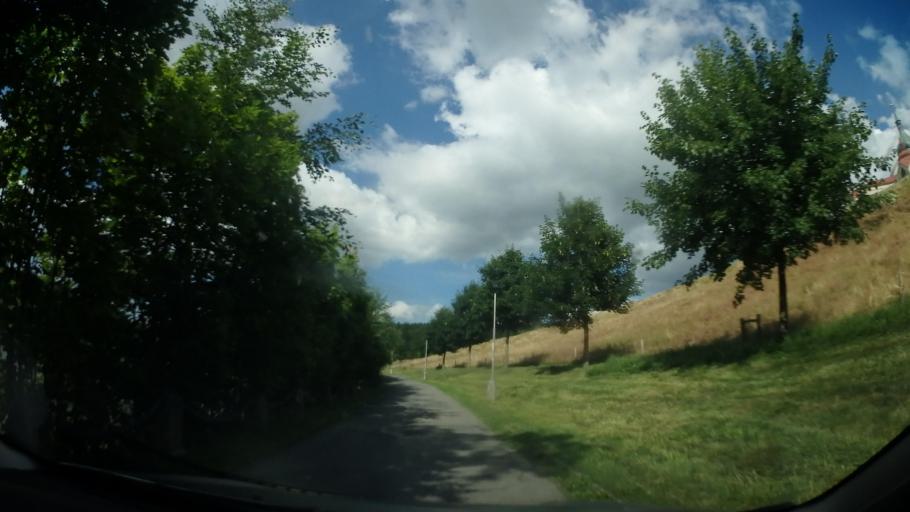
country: CZ
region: Vysocina
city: Zd'ar nad Sazavou Druhy
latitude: 49.5808
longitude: 15.9398
